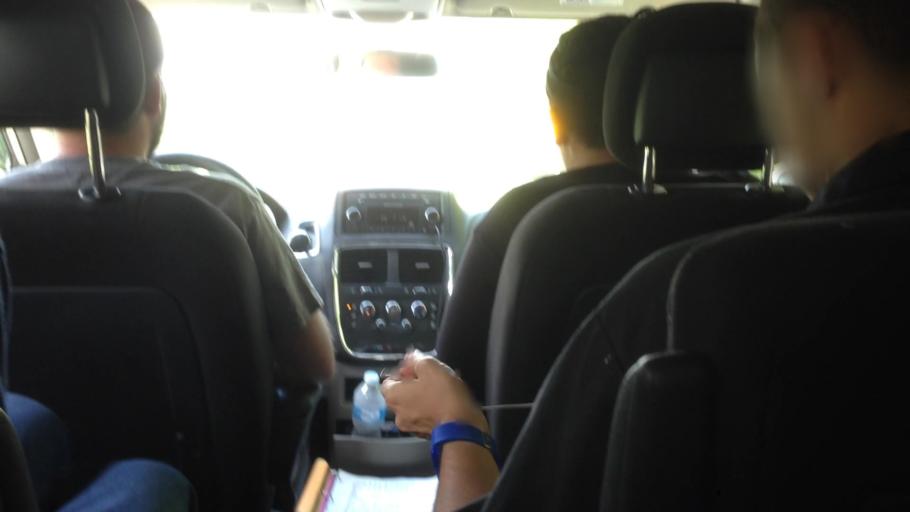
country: US
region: New York
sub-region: Dutchess County
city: Tivoli
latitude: 42.1181
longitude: -73.8911
